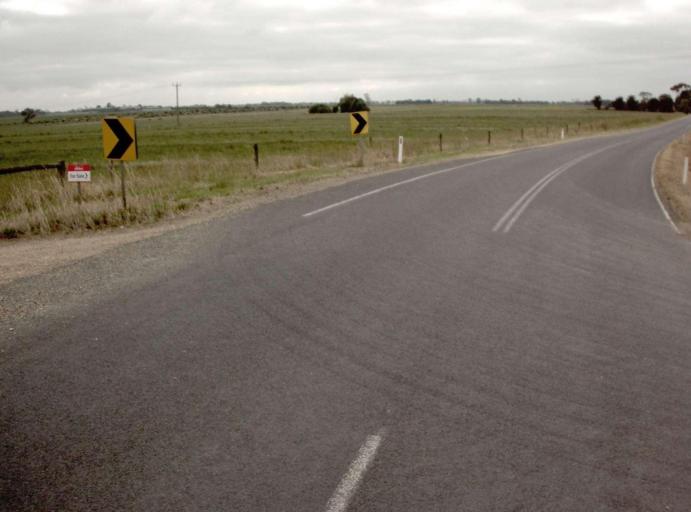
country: AU
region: Victoria
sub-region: Wellington
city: Heyfield
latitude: -38.0310
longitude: 146.9165
